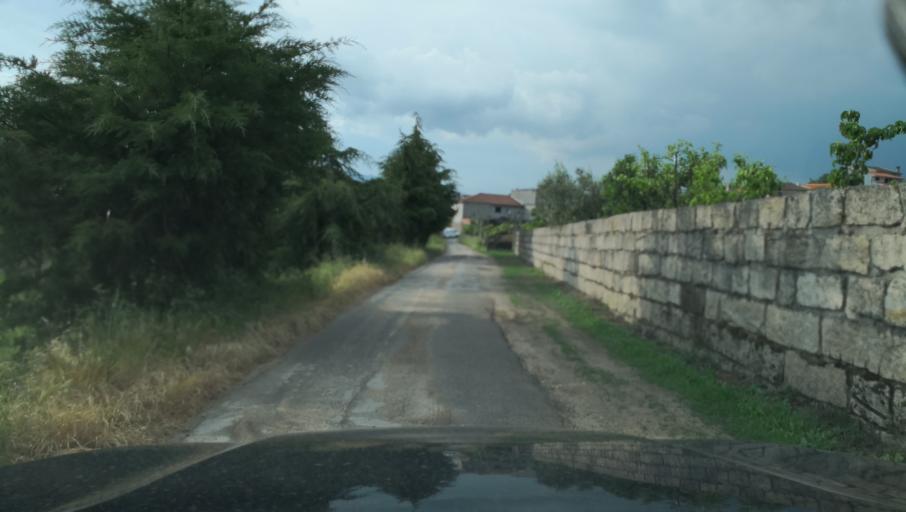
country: PT
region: Vila Real
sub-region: Vila Real
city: Vila Real
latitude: 41.3082
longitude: -7.6999
